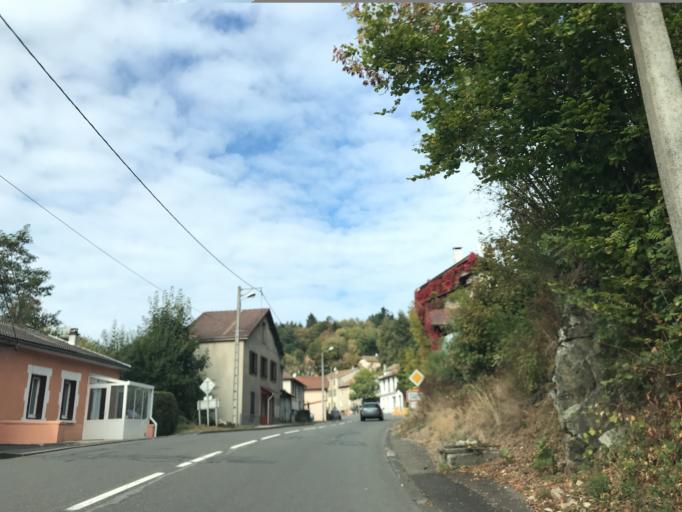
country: FR
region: Auvergne
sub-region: Departement du Puy-de-Dome
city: La Monnerie-le-Montel
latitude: 45.8657
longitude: 3.5881
